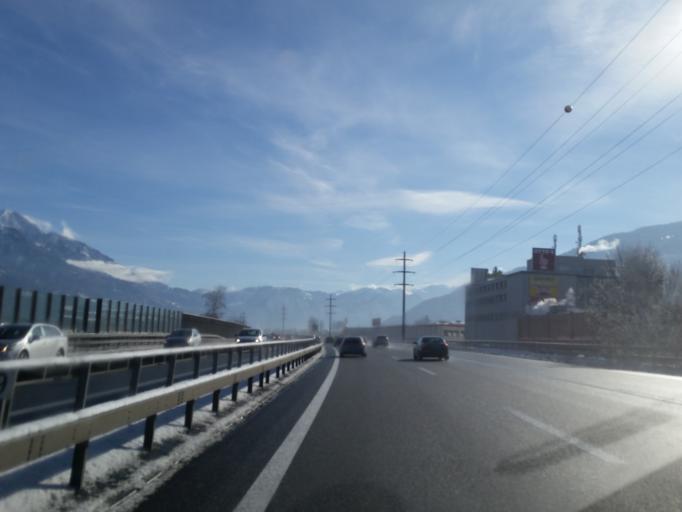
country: CH
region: Saint Gallen
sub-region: Wahlkreis Sarganserland
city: Sargans
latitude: 47.0416
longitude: 9.4375
